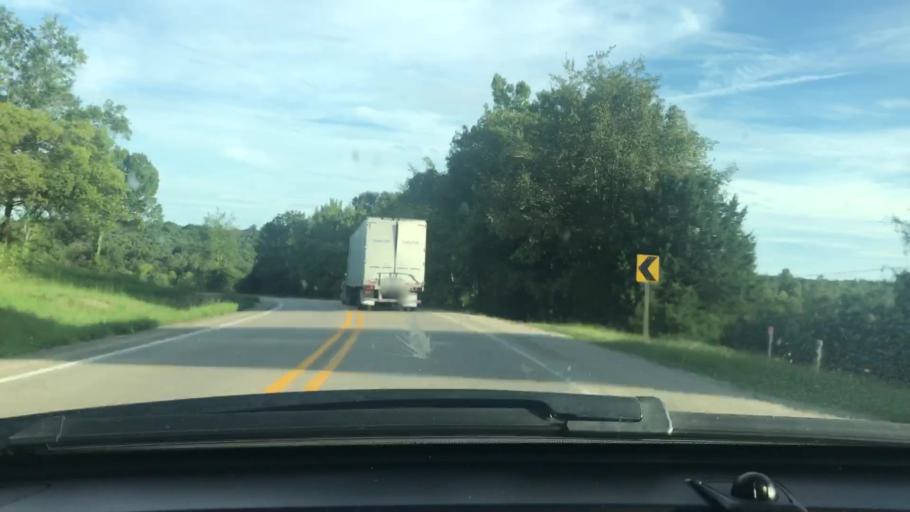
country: US
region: Arkansas
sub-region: Randolph County
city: Pocahontas
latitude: 36.2141
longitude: -91.2146
